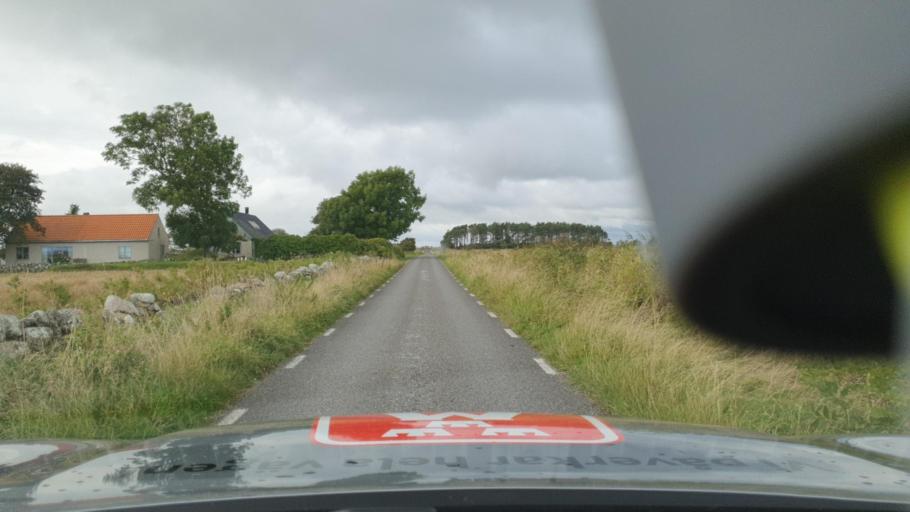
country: SE
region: Gotland
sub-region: Gotland
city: Hemse
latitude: 56.9994
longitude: 18.3784
